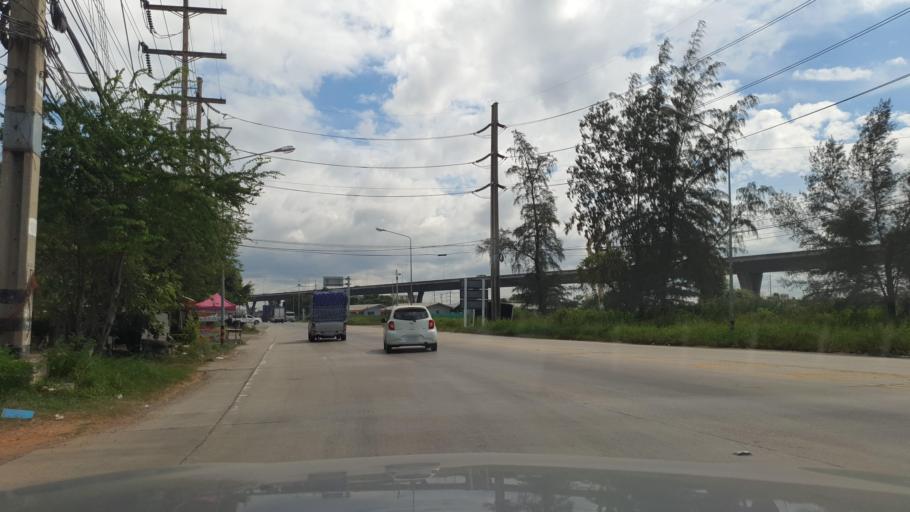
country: TH
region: Chachoengsao
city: Bang Pakong
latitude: 13.5129
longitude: 100.9879
